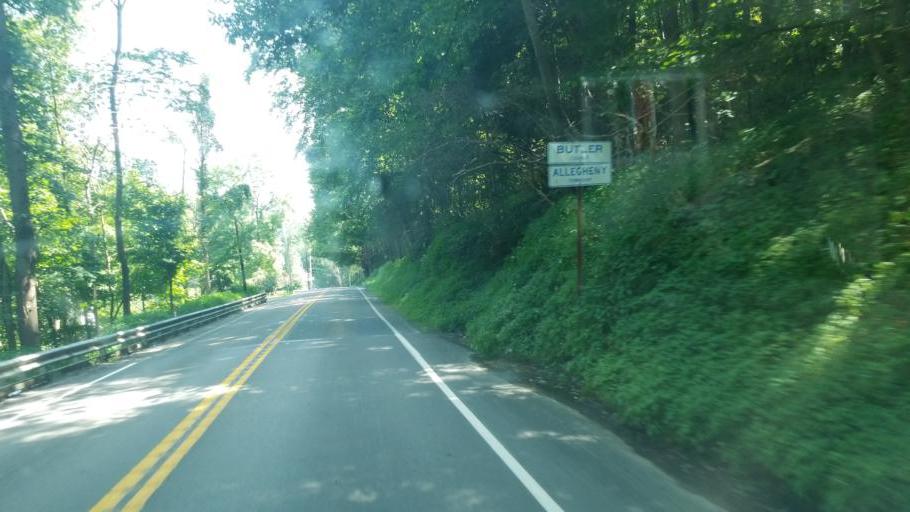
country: US
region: Pennsylvania
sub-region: Clarion County
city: Knox
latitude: 41.1729
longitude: -79.6971
